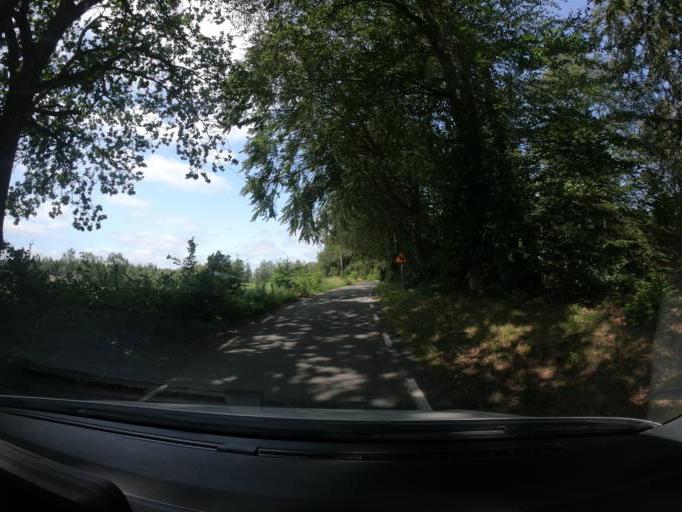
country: SE
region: Skane
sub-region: Hassleholms Kommun
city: Sosdala
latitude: 55.9512
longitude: 13.6466
